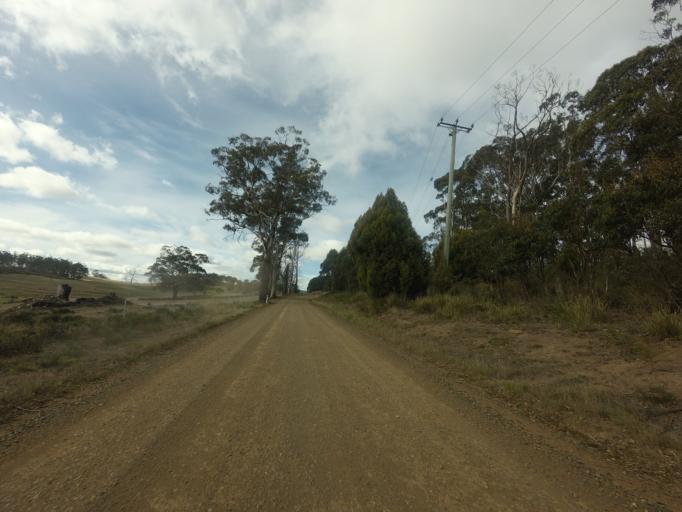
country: AU
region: Tasmania
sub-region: Brighton
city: Bridgewater
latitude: -42.3857
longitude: 147.4106
